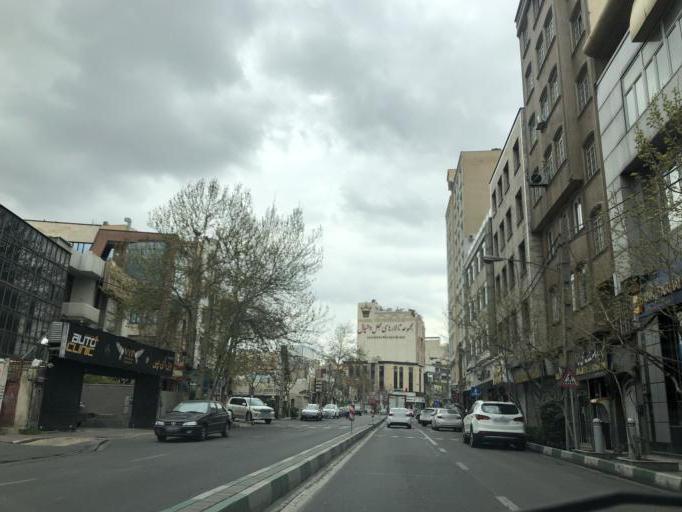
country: IR
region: Tehran
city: Tajrish
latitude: 35.7802
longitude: 51.4518
